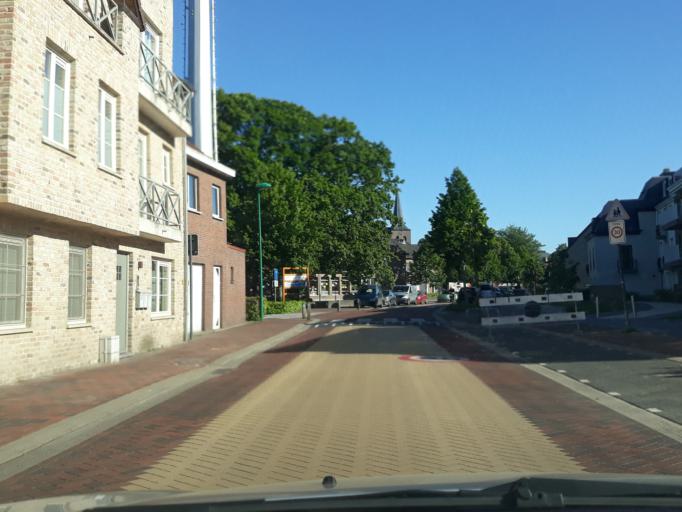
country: BE
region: Flanders
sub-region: Provincie Antwerpen
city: Vosselaar
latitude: 51.3106
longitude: 4.8871
